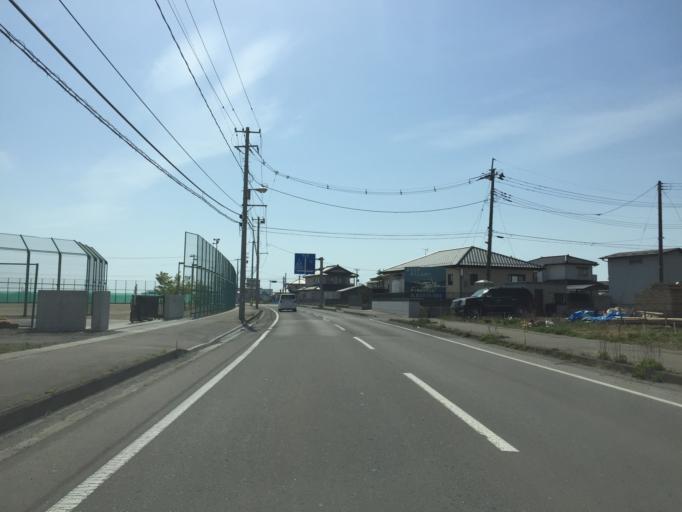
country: JP
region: Miyagi
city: Watari
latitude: 38.0424
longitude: 140.9079
